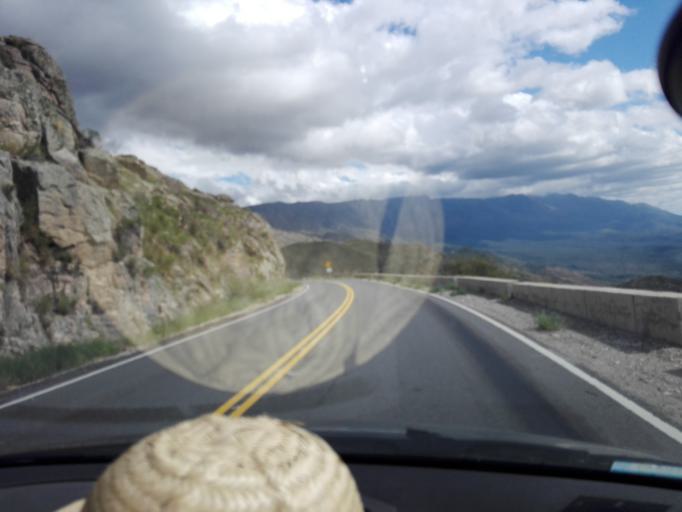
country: AR
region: Cordoba
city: Mina Clavero
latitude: -31.7753
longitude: -64.9142
